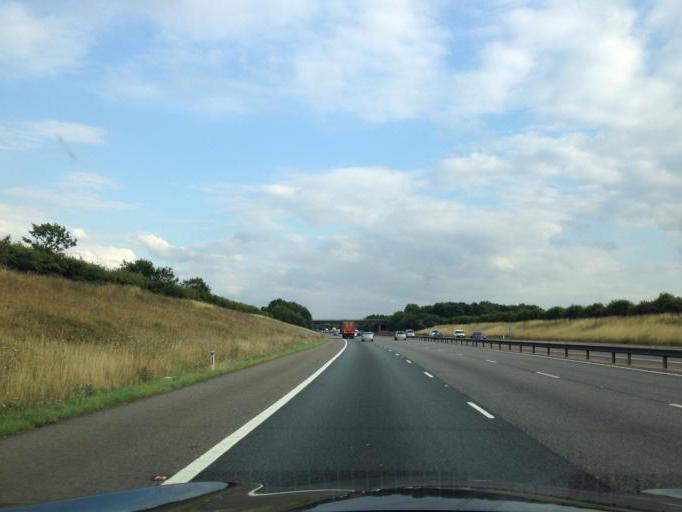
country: GB
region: England
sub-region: Warwickshire
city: Harbury
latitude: 52.1675
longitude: -1.4391
